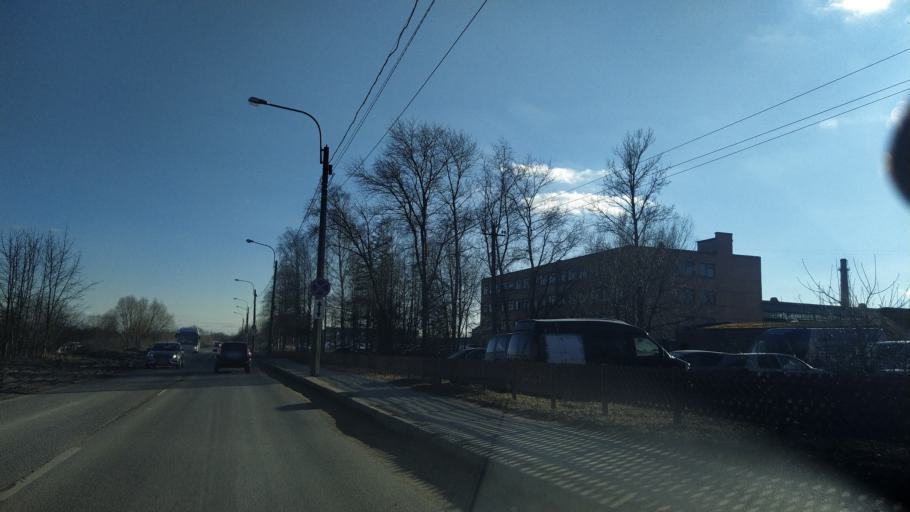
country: RU
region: St.-Petersburg
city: Pushkin
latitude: 59.6976
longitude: 30.3951
